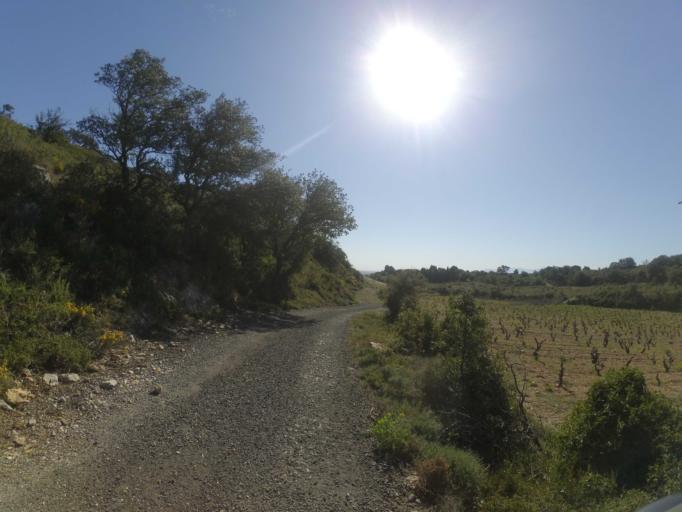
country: FR
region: Languedoc-Roussillon
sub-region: Departement des Pyrenees-Orientales
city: Baixas
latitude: 42.7616
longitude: 2.7665
